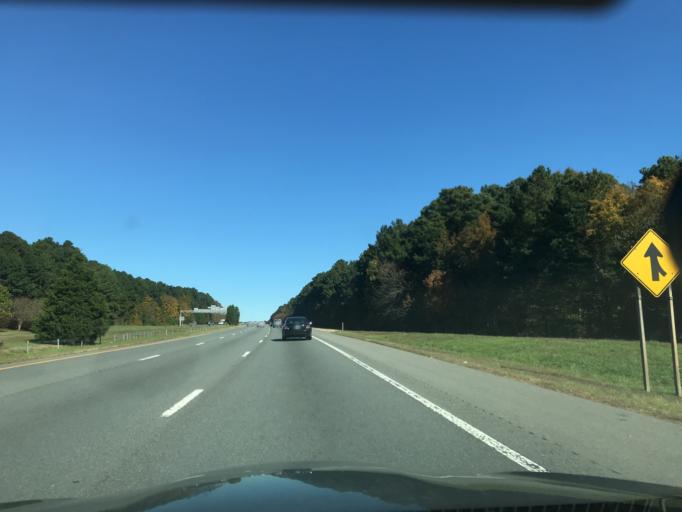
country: US
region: North Carolina
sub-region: Durham County
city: Durham
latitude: 35.9129
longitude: -78.8642
